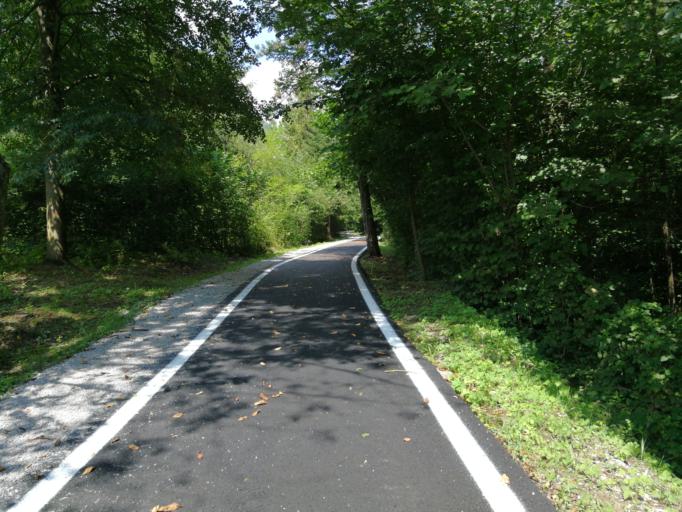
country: IT
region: Trentino-Alto Adige
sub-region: Provincia di Trento
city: Storo
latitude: 45.8646
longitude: 10.5820
